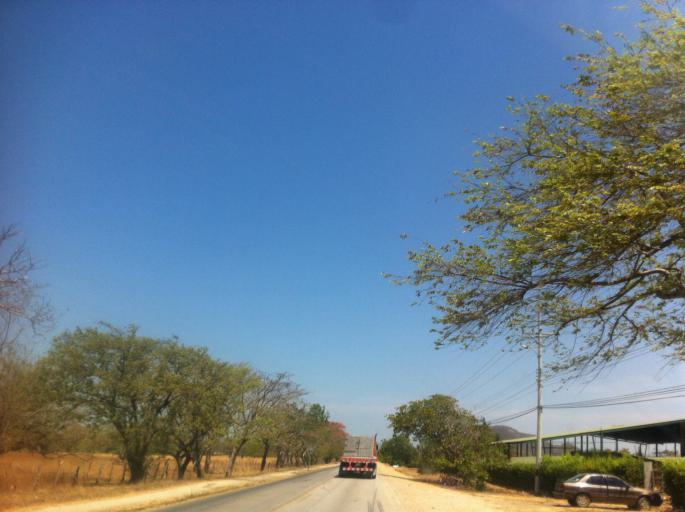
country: CR
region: Guanacaste
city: Santa Cruz
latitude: 10.2588
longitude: -85.5659
